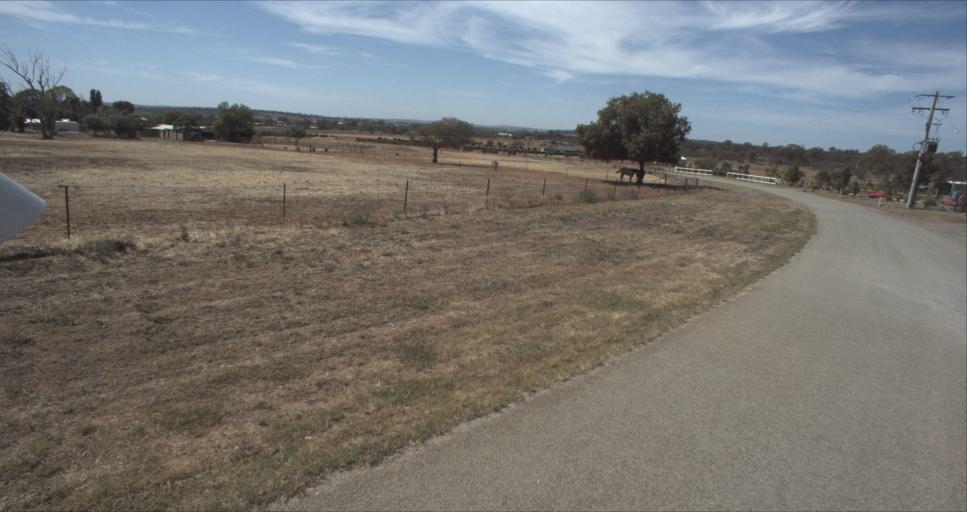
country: AU
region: New South Wales
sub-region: Leeton
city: Leeton
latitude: -34.5762
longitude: 146.4514
